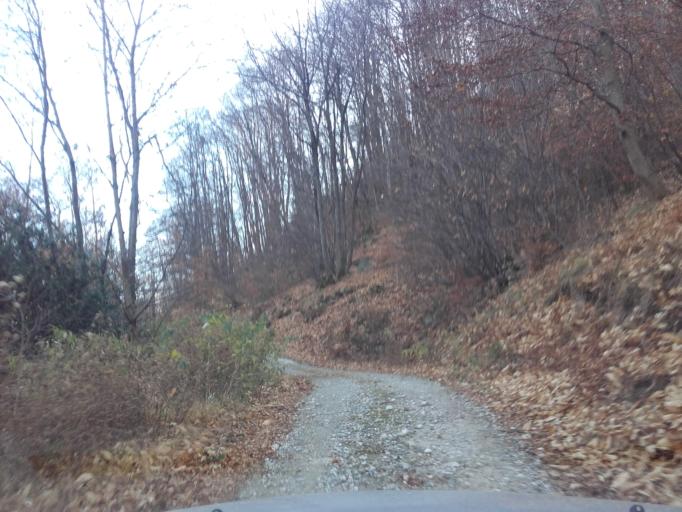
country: IT
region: Piedmont
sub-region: Provincia di Torino
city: Sparone
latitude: 45.4287
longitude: 7.5331
